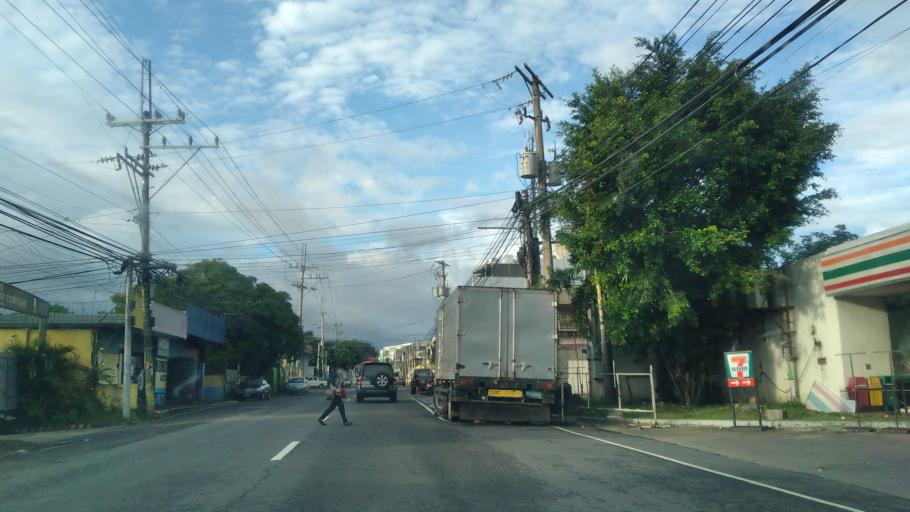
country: PH
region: Calabarzon
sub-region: Province of Quezon
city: Lucena
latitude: 13.9480
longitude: 121.6141
